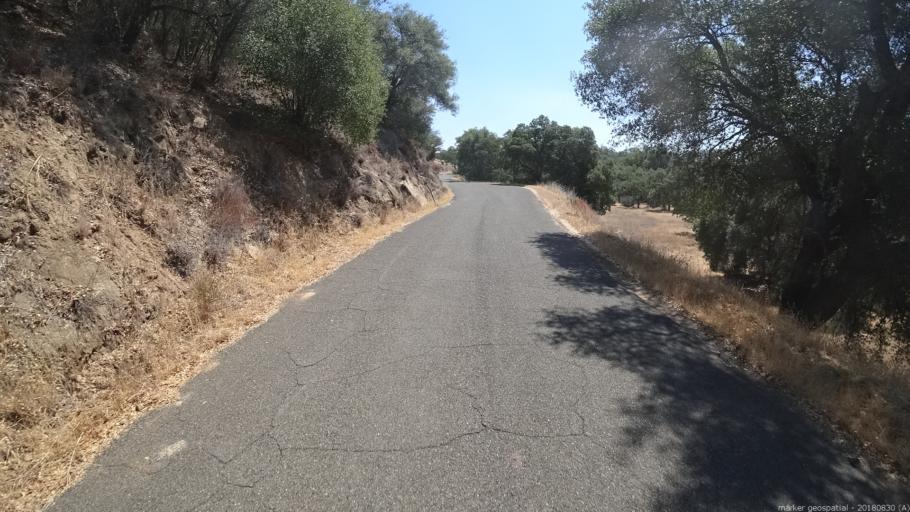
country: US
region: California
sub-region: Monterey County
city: King City
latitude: 35.9889
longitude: -121.3581
